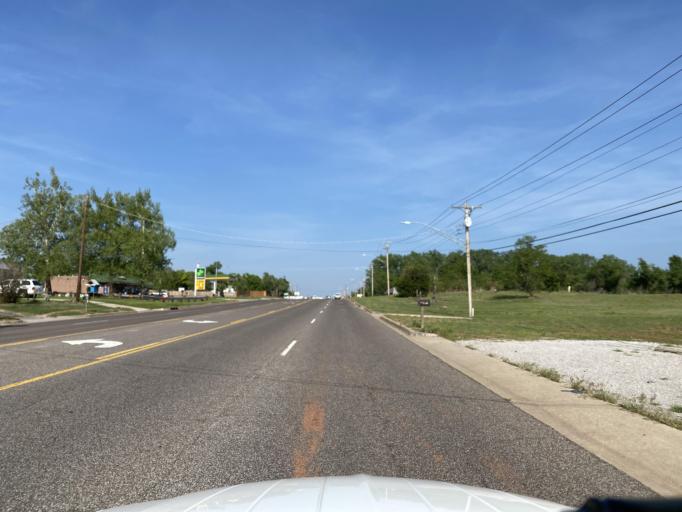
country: US
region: Oklahoma
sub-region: Oklahoma County
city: Spencer
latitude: 35.4930
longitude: -97.3611
